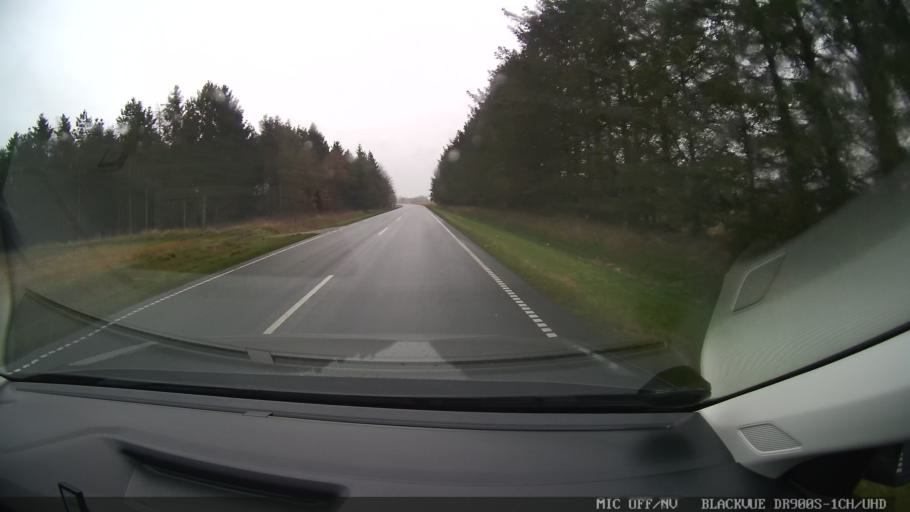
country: DK
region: Central Jutland
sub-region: Herning Kommune
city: Sunds
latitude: 56.2804
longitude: 8.9486
